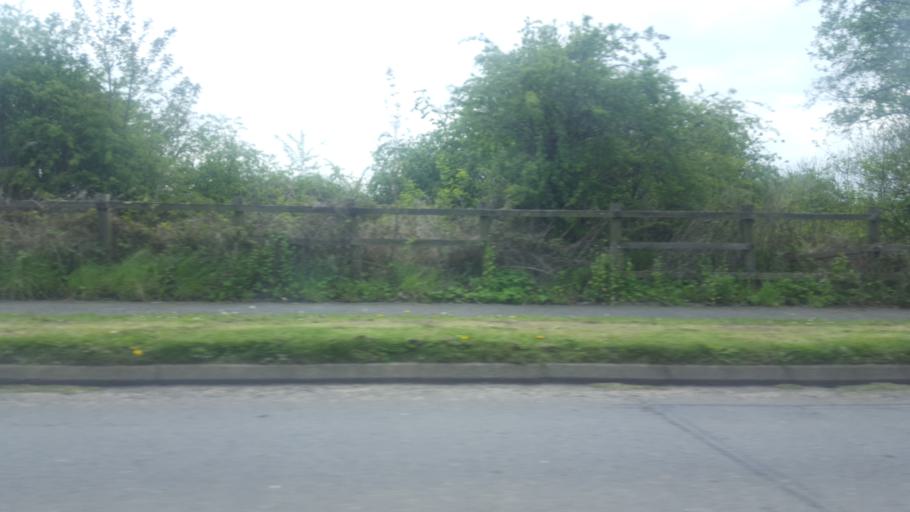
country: GB
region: Scotland
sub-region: Falkirk
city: Polmont
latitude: 56.0013
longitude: -3.7075
